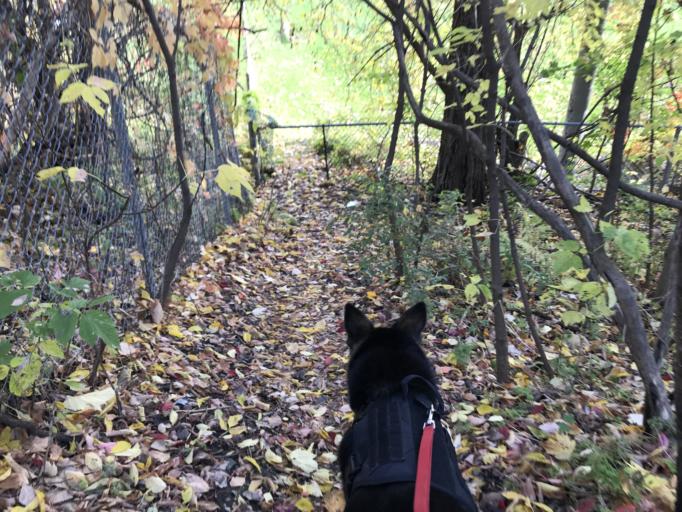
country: CA
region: Quebec
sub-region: Laurentides
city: Sainte-Therese
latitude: 45.6468
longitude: -73.8457
